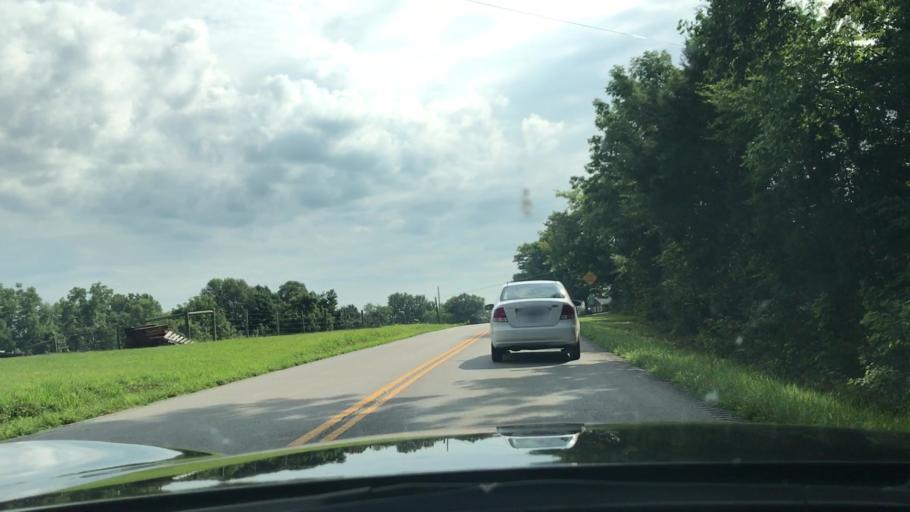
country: US
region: Kentucky
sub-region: Green County
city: Greensburg
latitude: 37.2712
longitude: -85.5305
